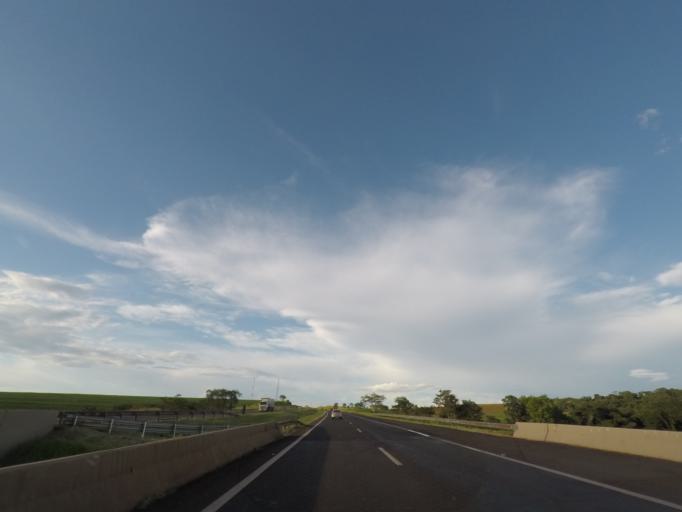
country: BR
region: Sao Paulo
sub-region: Ituverava
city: Ituverava
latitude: -20.2796
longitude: -47.7973
